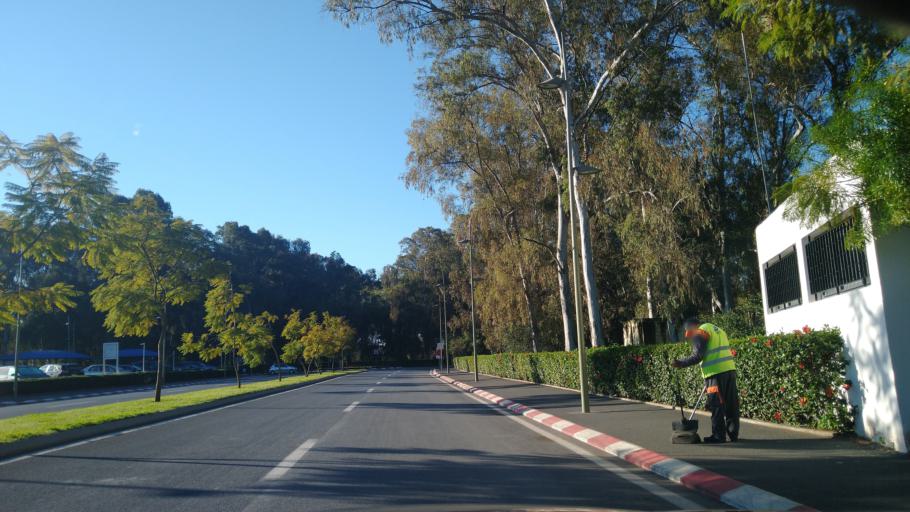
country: MA
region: Rabat-Sale-Zemmour-Zaer
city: Sale
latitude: 34.0349
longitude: -6.7495
